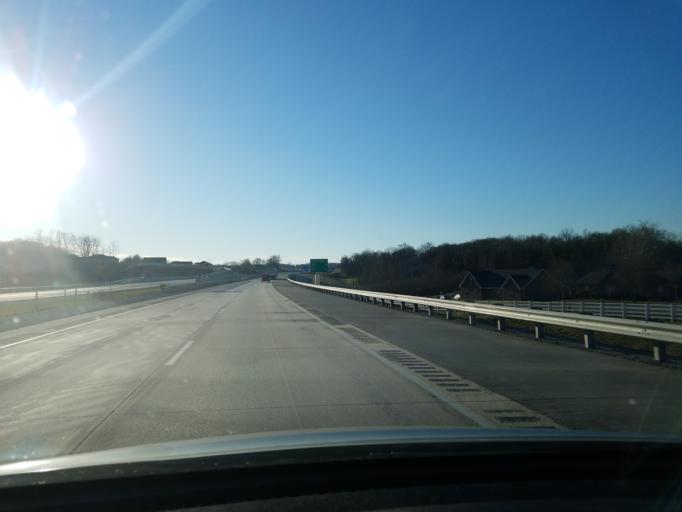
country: US
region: Indiana
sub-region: Clark County
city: Oak Park
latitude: 38.3454
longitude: -85.6798
